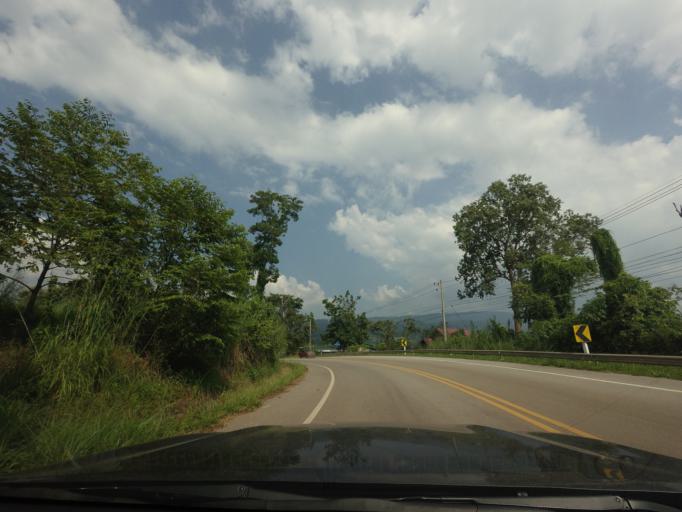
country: TH
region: Phitsanulok
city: Nakhon Thai
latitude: 17.0171
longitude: 100.9172
